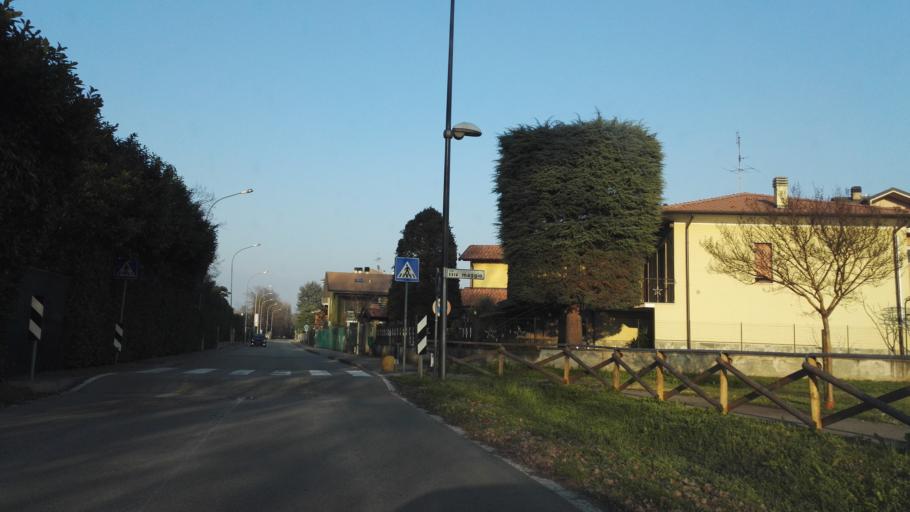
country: IT
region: Lombardy
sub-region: Citta metropolitana di Milano
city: Tribiano
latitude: 45.4104
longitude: 9.3763
